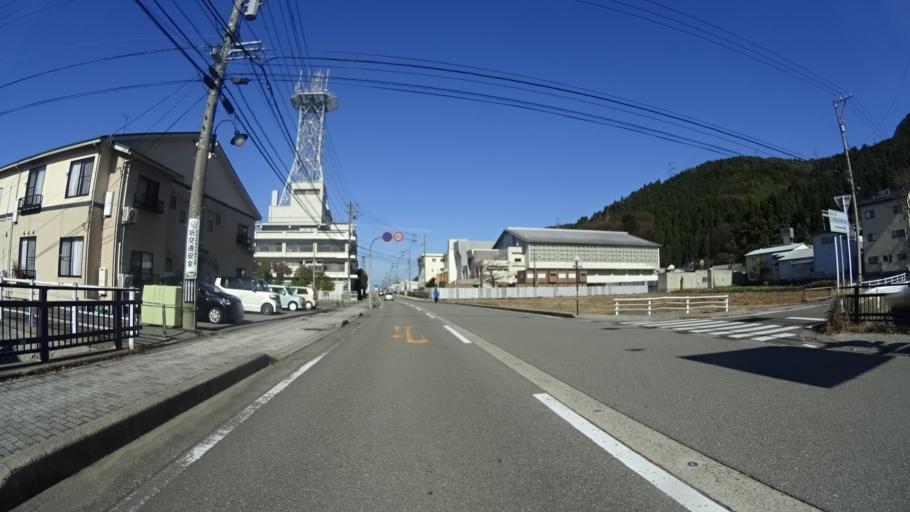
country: JP
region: Ishikawa
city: Tsurugi-asahimachi
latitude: 36.4529
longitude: 136.6249
